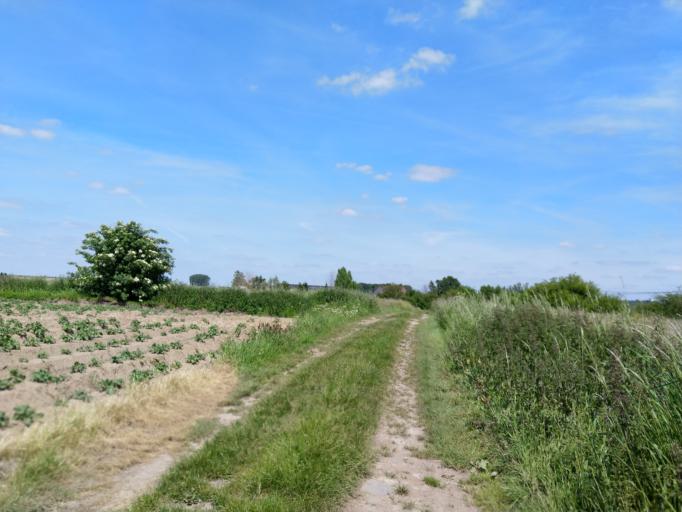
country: BE
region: Wallonia
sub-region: Province du Hainaut
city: Roeulx
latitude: 50.5019
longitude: 4.0639
